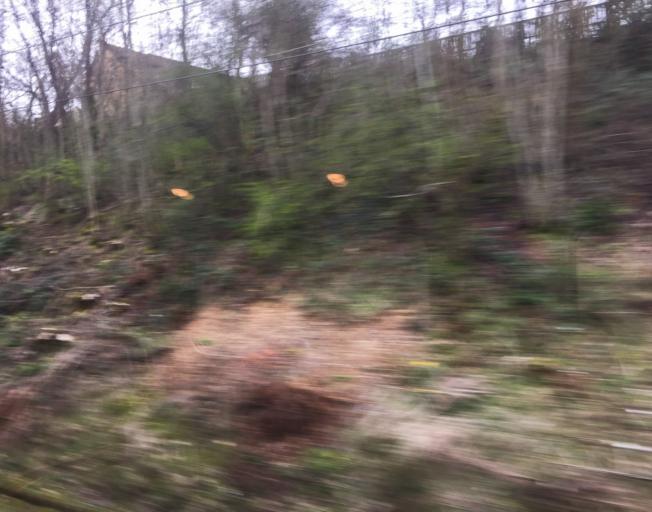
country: GB
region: Scotland
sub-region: West Dunbartonshire
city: Old Kilpatrick
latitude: 55.9215
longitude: -4.4486
